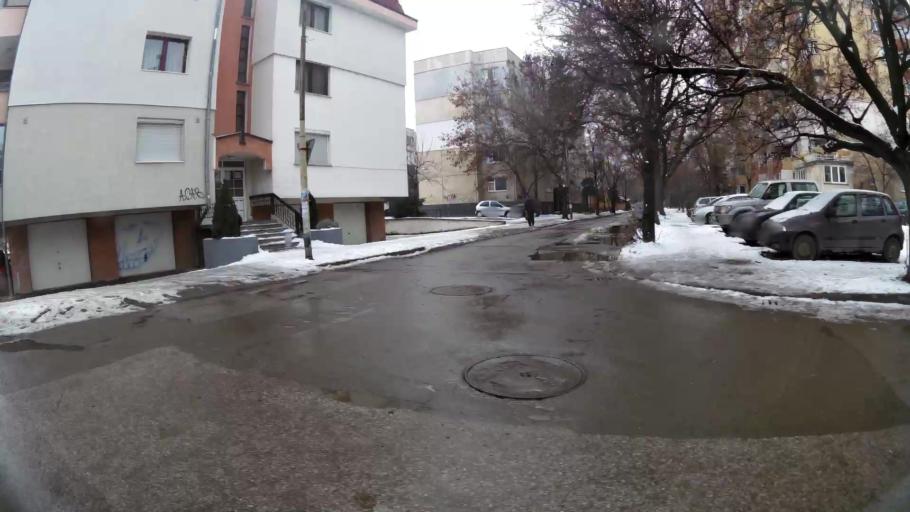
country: BG
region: Sofia-Capital
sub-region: Stolichna Obshtina
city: Sofia
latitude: 42.7021
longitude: 23.3658
